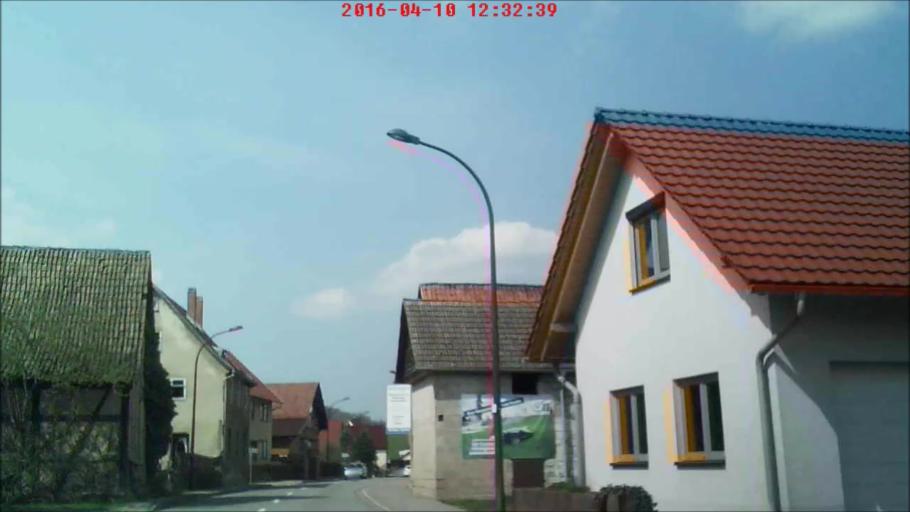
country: DE
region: Thuringia
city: Breitenbach
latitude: 50.7006
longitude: 10.4851
